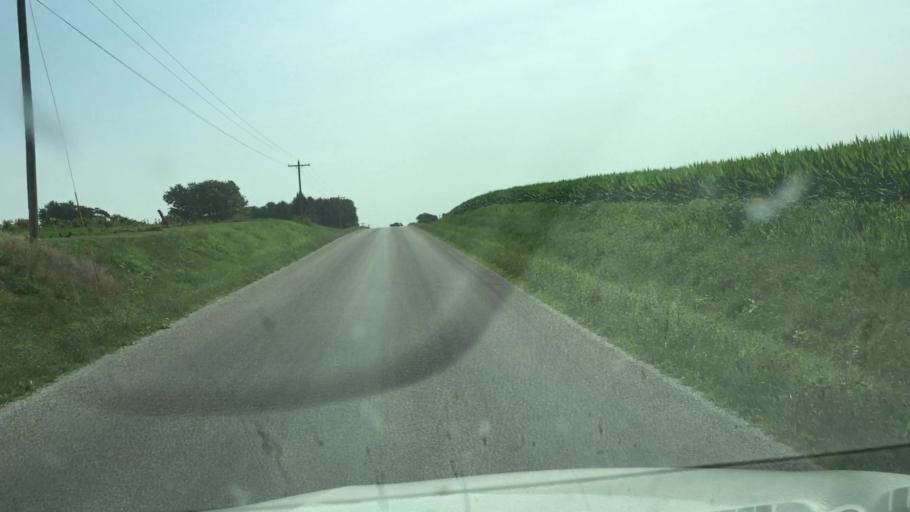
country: US
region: Illinois
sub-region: Hancock County
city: Nauvoo
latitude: 40.5114
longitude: -91.3462
